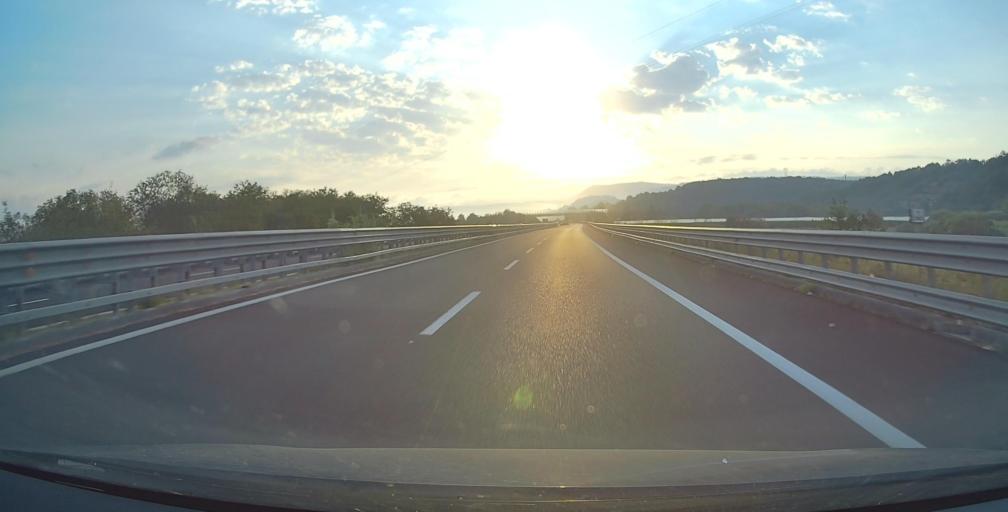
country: IT
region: Calabria
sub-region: Provincia di Reggio Calabria
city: Rosarno
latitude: 38.4991
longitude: 16.0229
